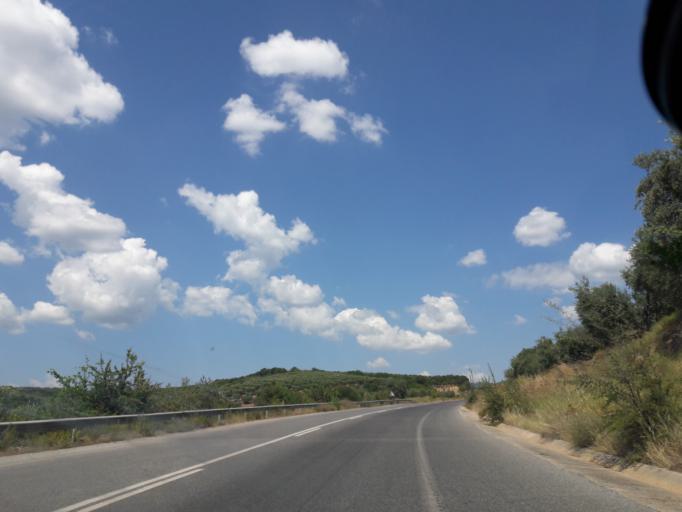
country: GR
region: Central Macedonia
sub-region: Nomos Chalkidikis
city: Megali Panagia
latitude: 40.3728
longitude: 23.6263
